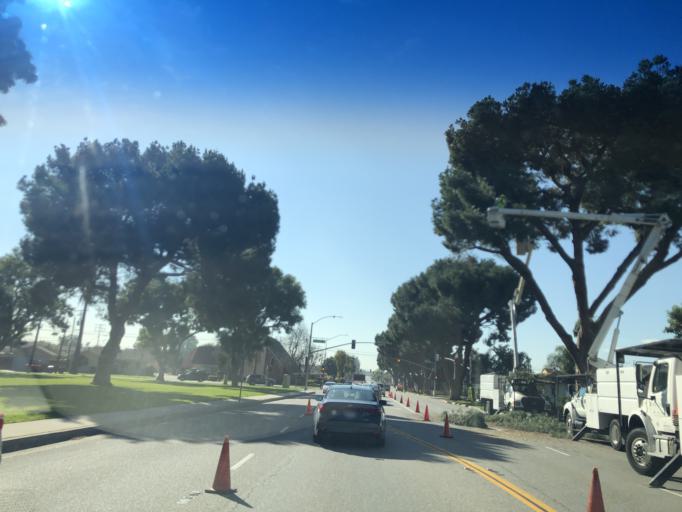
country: US
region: California
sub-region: Los Angeles County
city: South Whittier
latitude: 33.9441
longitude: -118.0248
